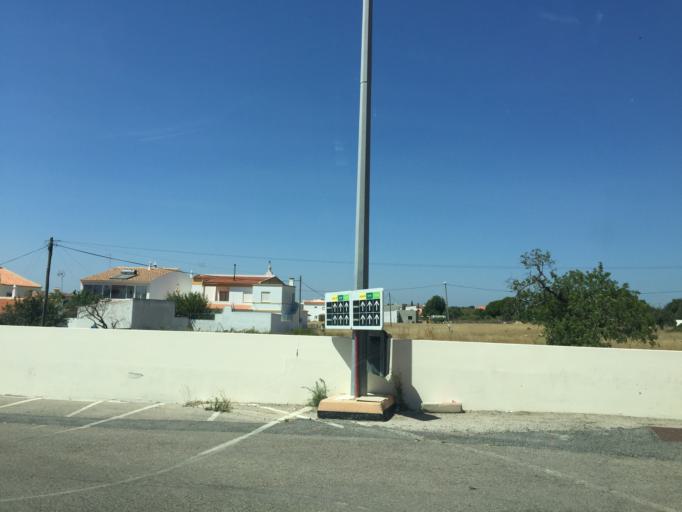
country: PT
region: Faro
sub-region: Albufeira
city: Ferreiras
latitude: 37.1268
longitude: -8.2375
